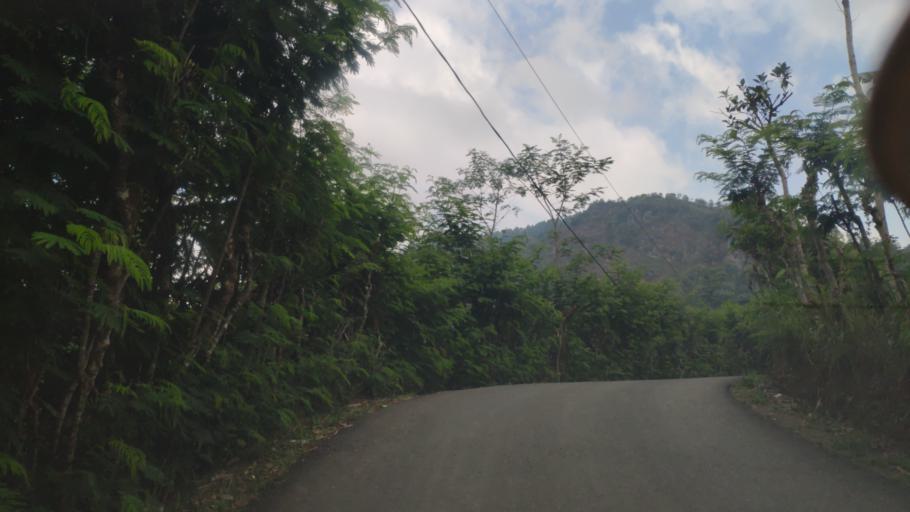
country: ID
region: Central Java
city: Wonosobo
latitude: -7.3026
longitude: 109.7655
